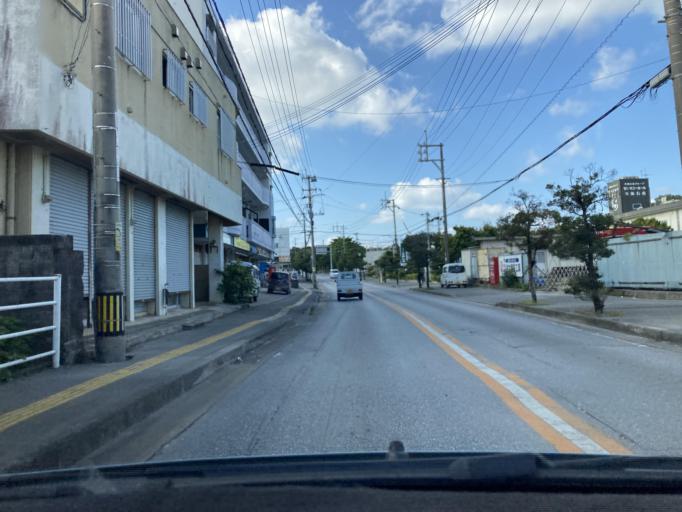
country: JP
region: Okinawa
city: Tomigusuku
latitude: 26.1845
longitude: 127.6866
